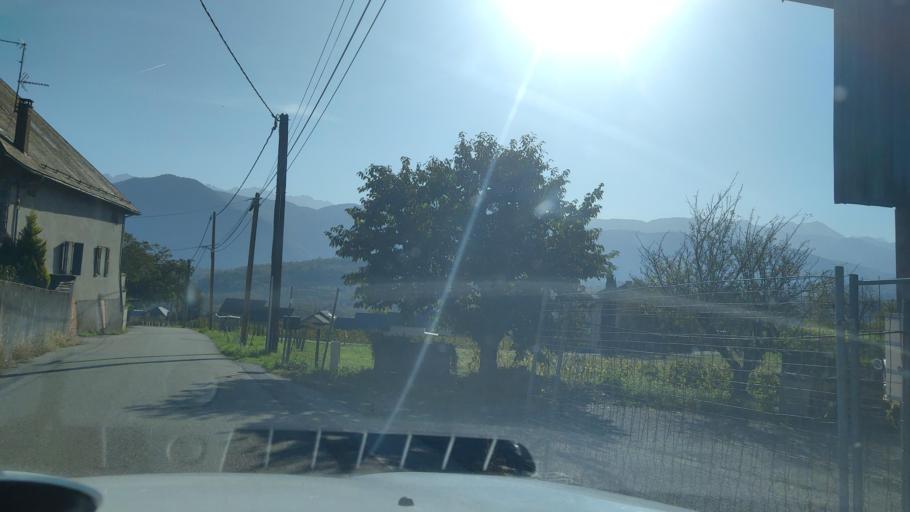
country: FR
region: Rhone-Alpes
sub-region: Departement de la Savoie
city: Coise-Saint-Jean-Pied-Gauthier
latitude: 45.5648
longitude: 6.1636
